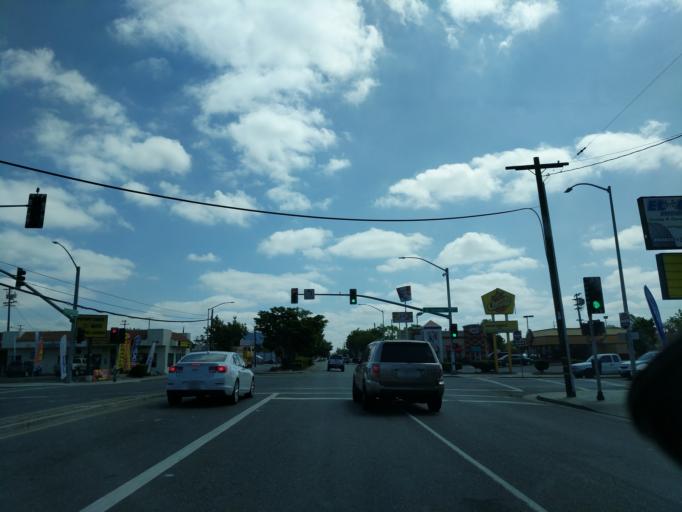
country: US
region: California
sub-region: San Joaquin County
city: Stockton
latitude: 37.9389
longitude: -121.2865
